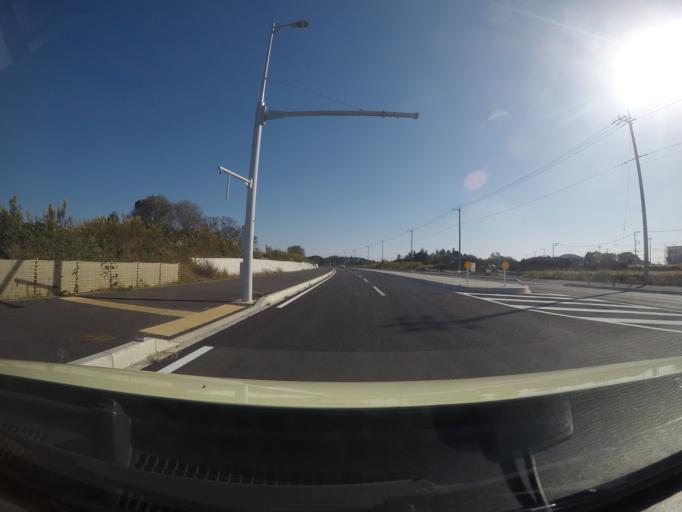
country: JP
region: Ibaraki
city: Naka
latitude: 36.1006
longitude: 140.1255
